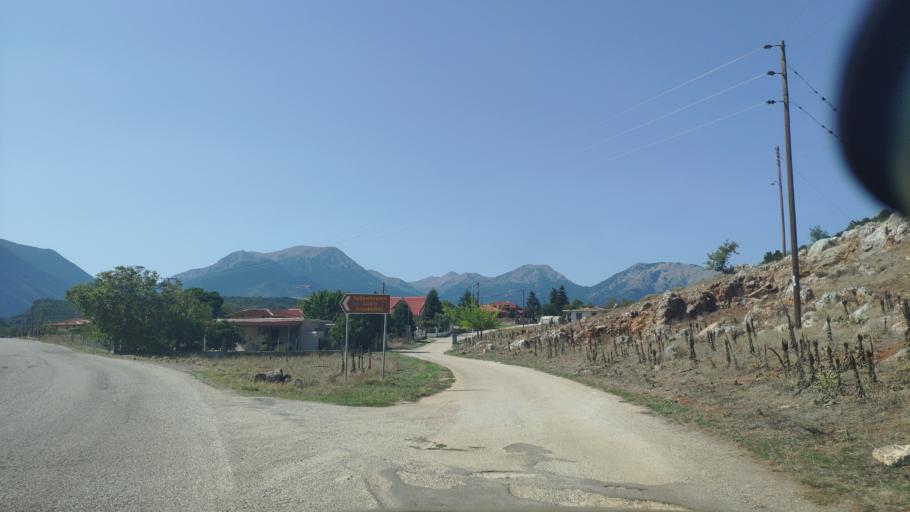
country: GR
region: Peloponnese
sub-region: Nomos Korinthias
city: Nemea
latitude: 37.8672
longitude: 22.4575
